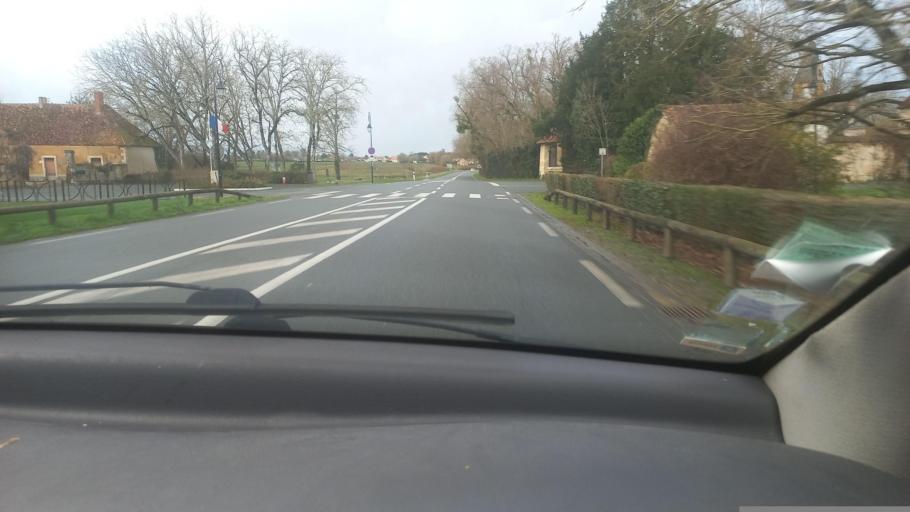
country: FR
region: Centre
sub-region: Departement de l'Indre
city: Neuvy-Pailloux
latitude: 46.8272
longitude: 1.8291
